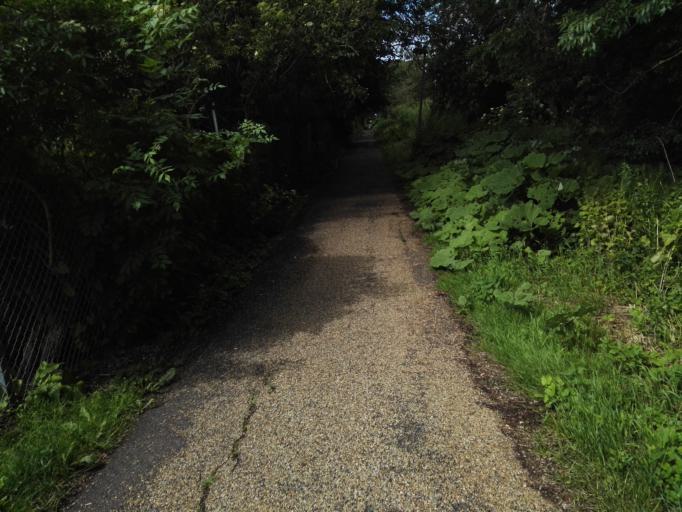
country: DK
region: Capital Region
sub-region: Frederikssund Kommune
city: Slangerup
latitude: 55.8459
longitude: 12.1801
